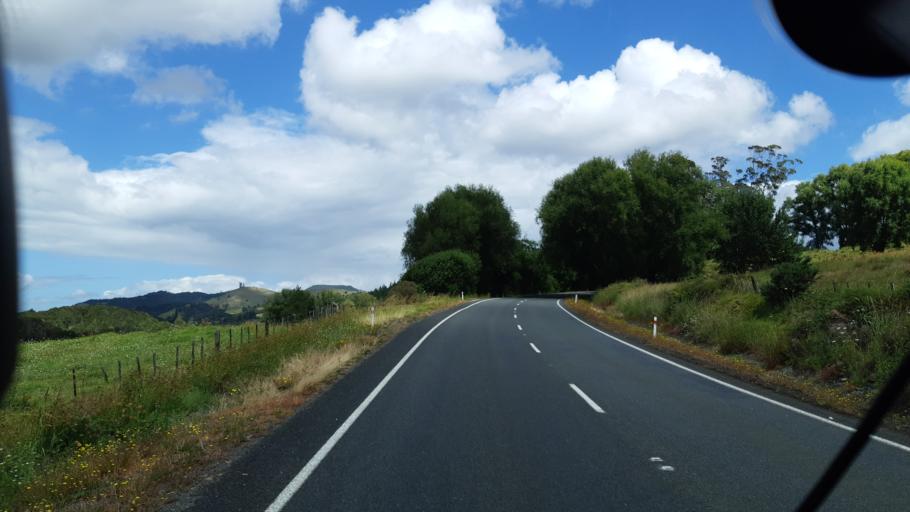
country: NZ
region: Northland
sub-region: Far North District
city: Taipa
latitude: -35.2548
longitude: 173.5563
